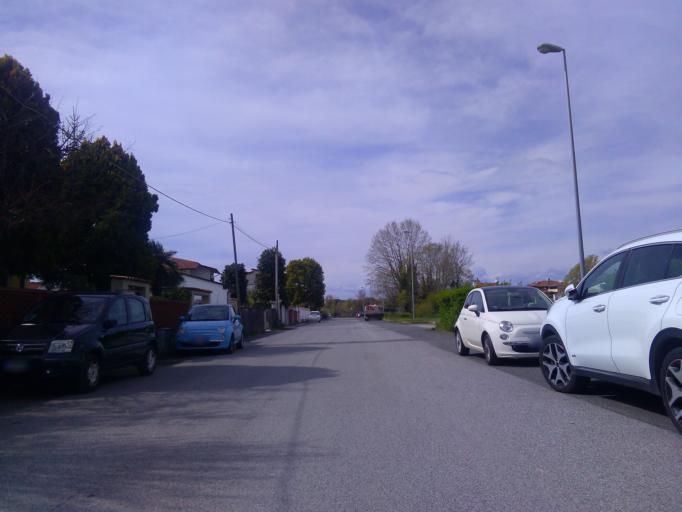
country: IT
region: Tuscany
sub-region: Provincia di Massa-Carrara
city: Marina di Carrara
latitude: 44.0456
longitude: 10.0414
